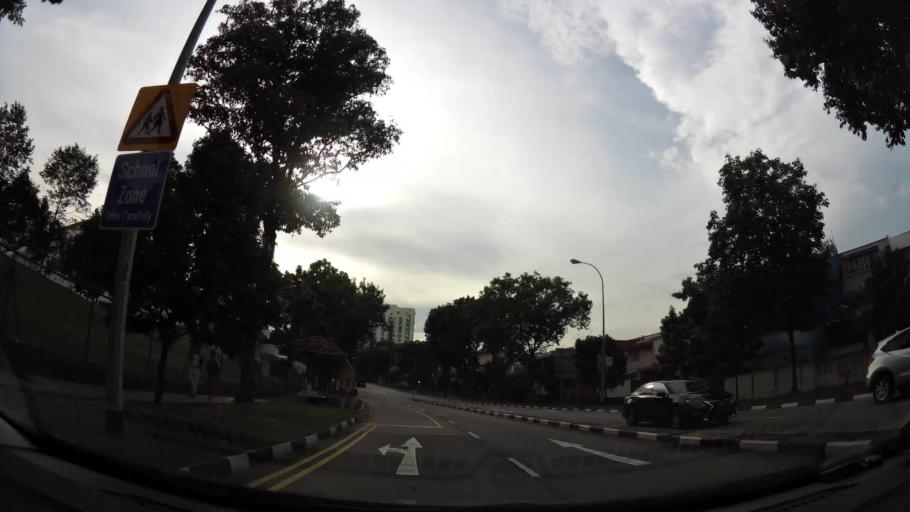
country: SG
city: Singapore
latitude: 1.3487
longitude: 103.8461
